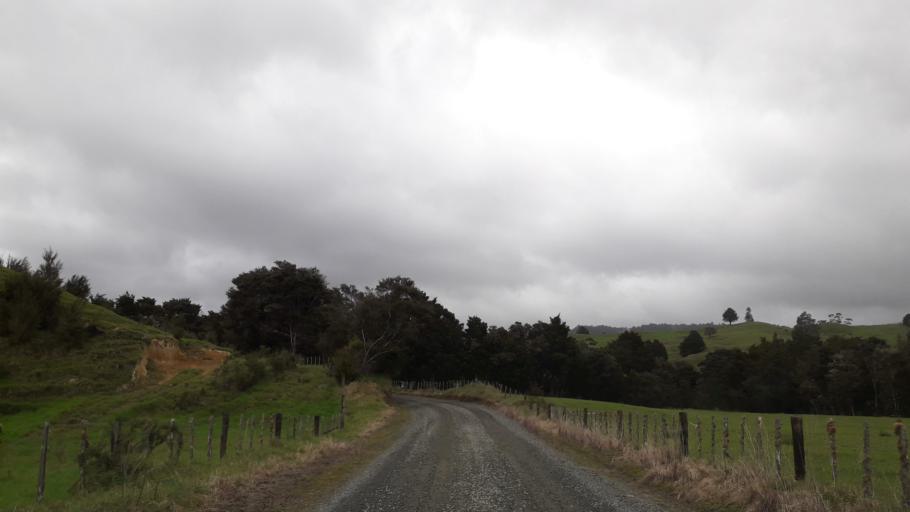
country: NZ
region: Northland
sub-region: Far North District
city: Waimate North
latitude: -35.1502
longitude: 173.7120
